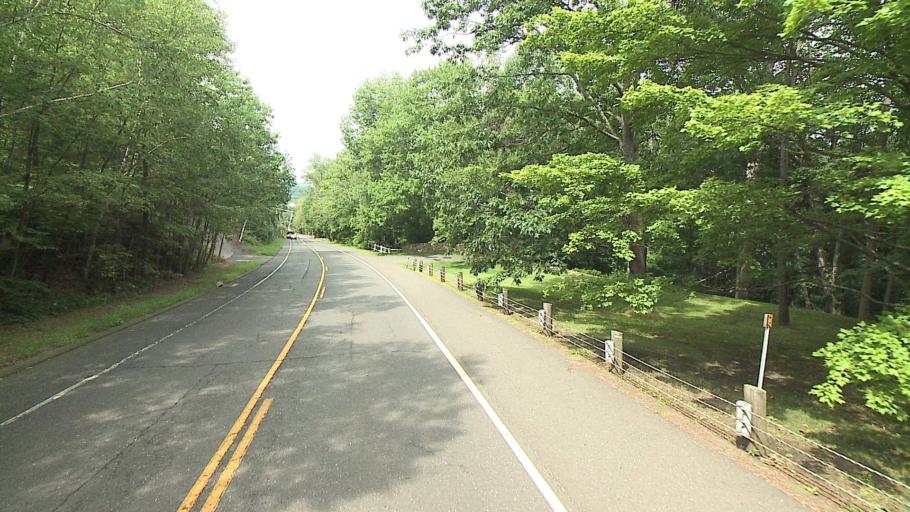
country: US
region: Connecticut
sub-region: Litchfield County
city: Woodbury
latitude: 41.5633
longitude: -73.2962
